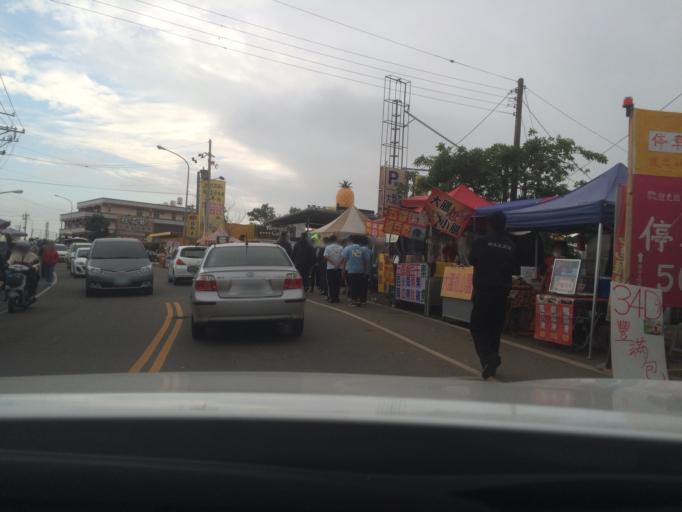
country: TW
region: Taiwan
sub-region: Nantou
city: Nantou
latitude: 23.9337
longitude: 120.6378
